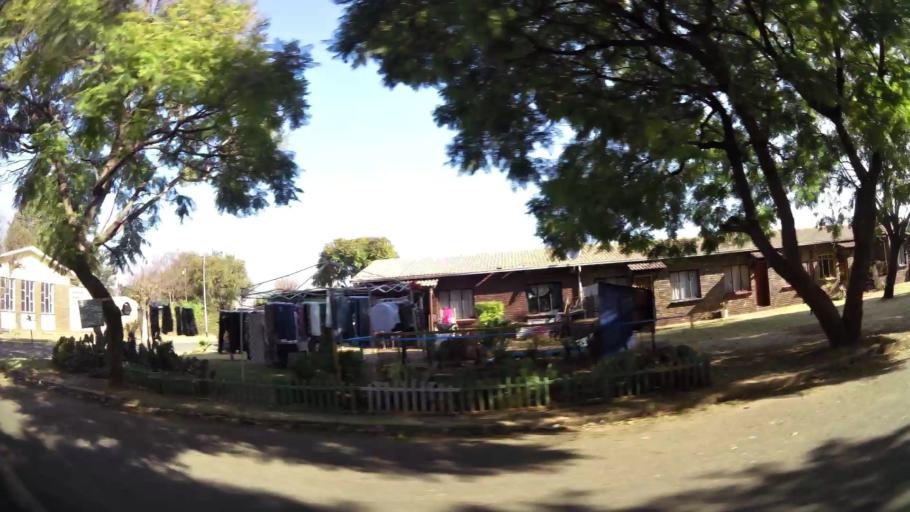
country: ZA
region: Gauteng
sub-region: West Rand District Municipality
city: Randfontein
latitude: -26.1704
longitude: 27.7108
